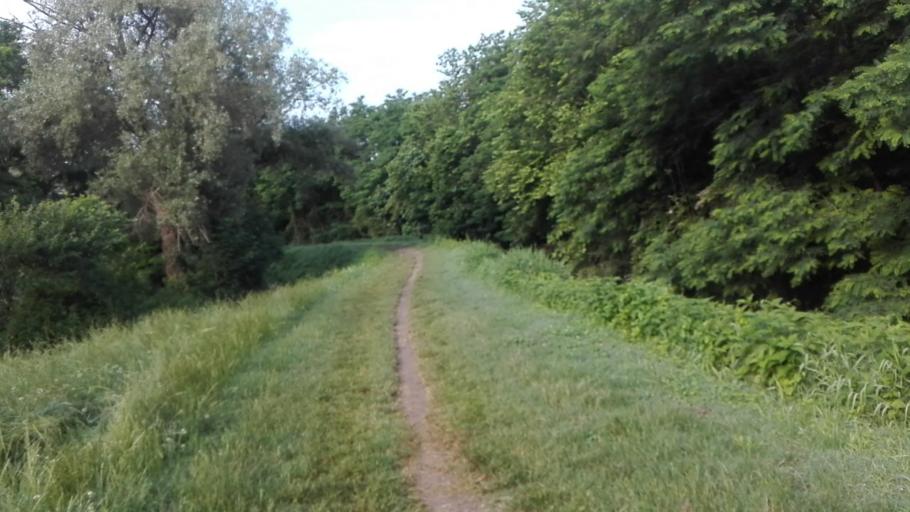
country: IT
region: Emilia-Romagna
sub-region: Provincia di Bologna
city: Bologna
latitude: 44.5251
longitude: 11.3373
